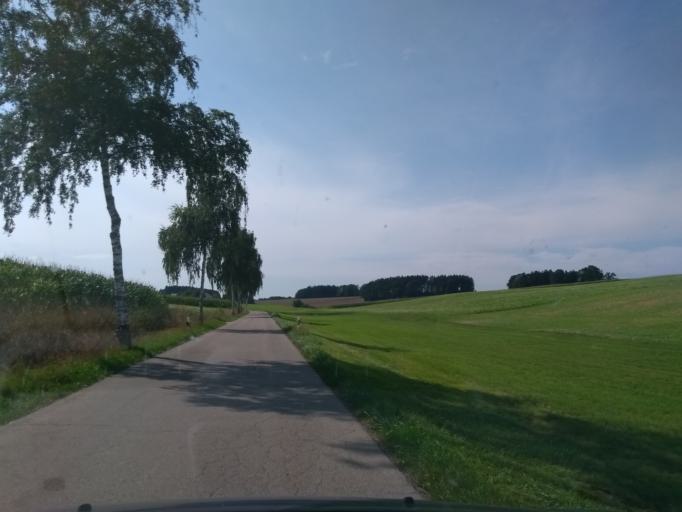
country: DE
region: Bavaria
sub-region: Upper Bavaria
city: Schwabhausen
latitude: 48.4017
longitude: 11.3664
